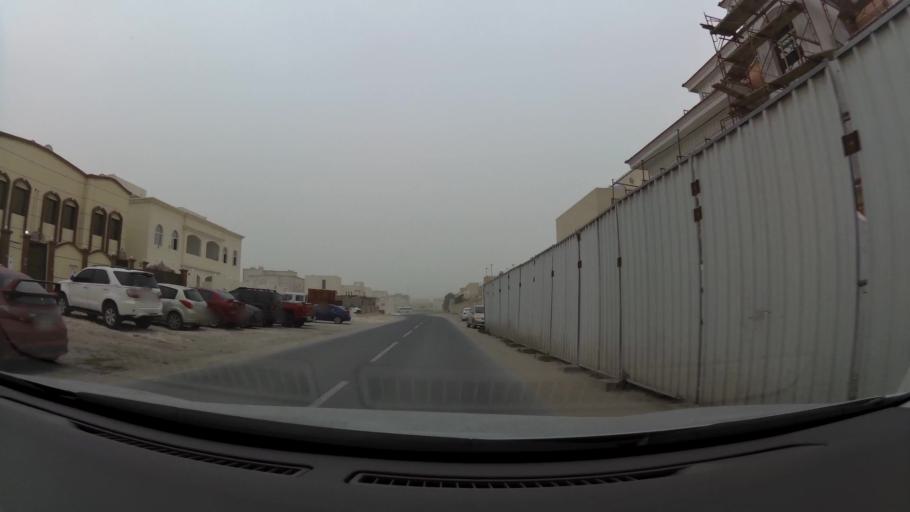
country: QA
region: Baladiyat ad Dawhah
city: Doha
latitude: 25.2463
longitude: 51.4857
